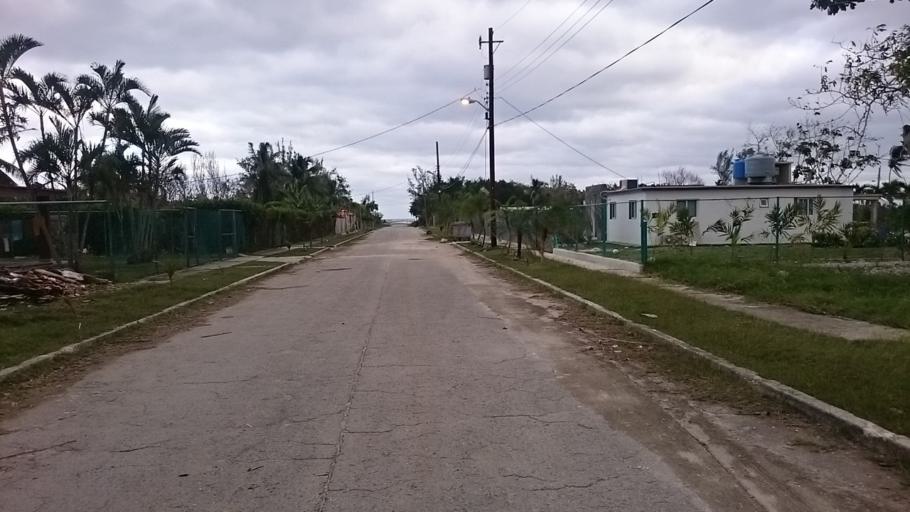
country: CU
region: Mayabeque
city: Jaruco
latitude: 23.1721
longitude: -82.1072
